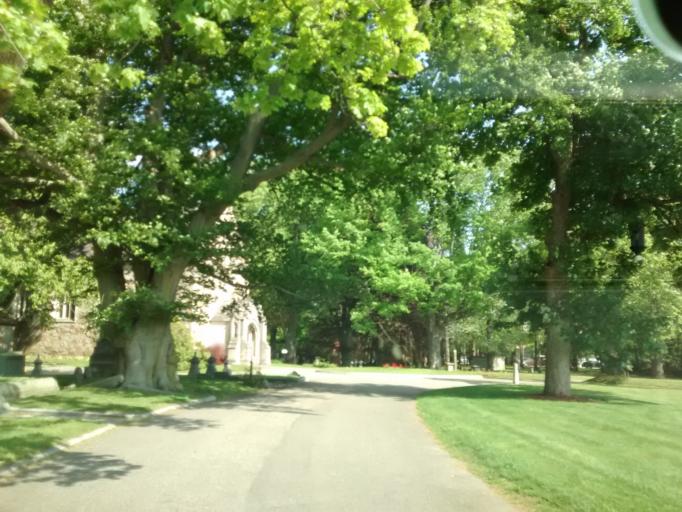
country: US
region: Massachusetts
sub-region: Worcester County
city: Worcester
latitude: 42.2797
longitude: -71.8043
